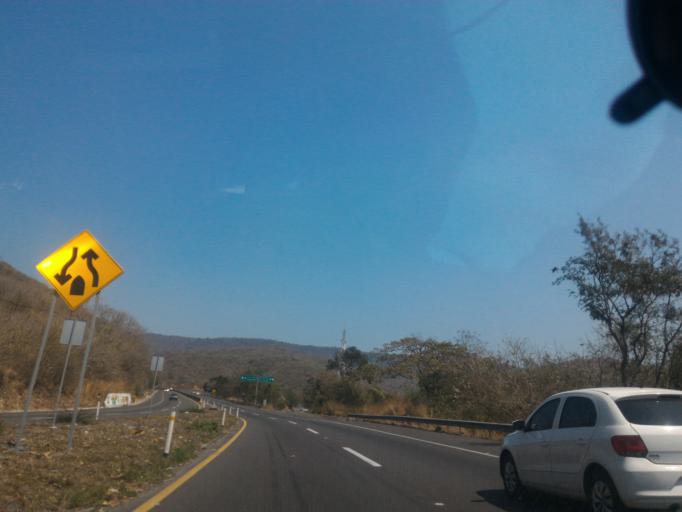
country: MX
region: Colima
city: Ixtlahuacan
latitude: 19.0250
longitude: -103.7989
